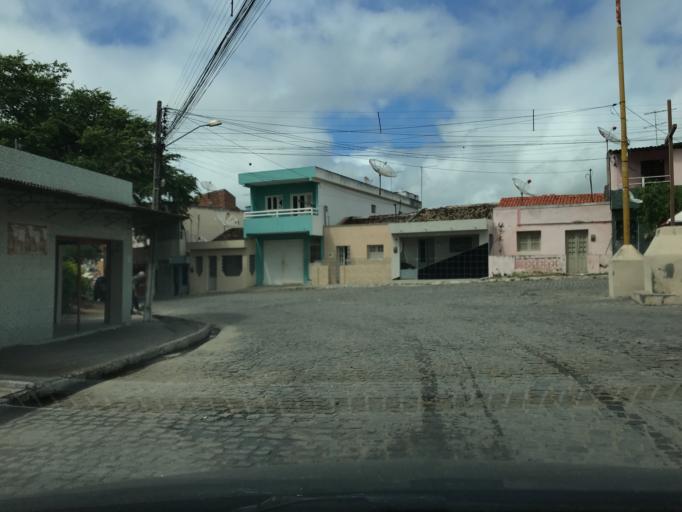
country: BR
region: Pernambuco
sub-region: Bezerros
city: Bezerros
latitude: -8.2330
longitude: -35.7583
